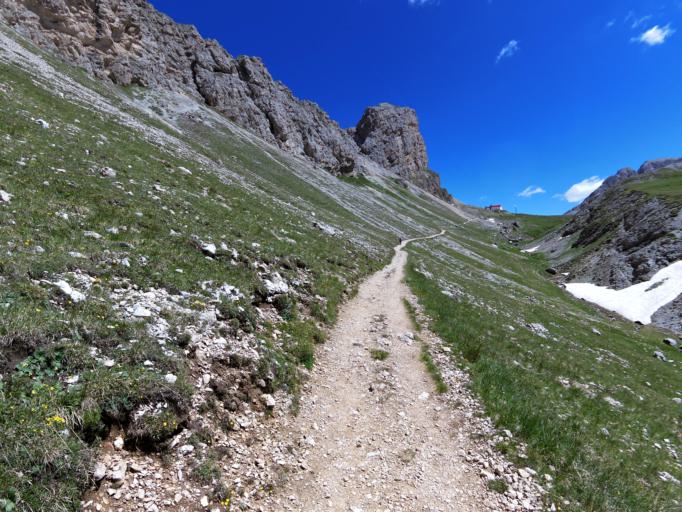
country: IT
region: Trentino-Alto Adige
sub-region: Bolzano
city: Siusi
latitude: 46.4973
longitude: 11.6235
